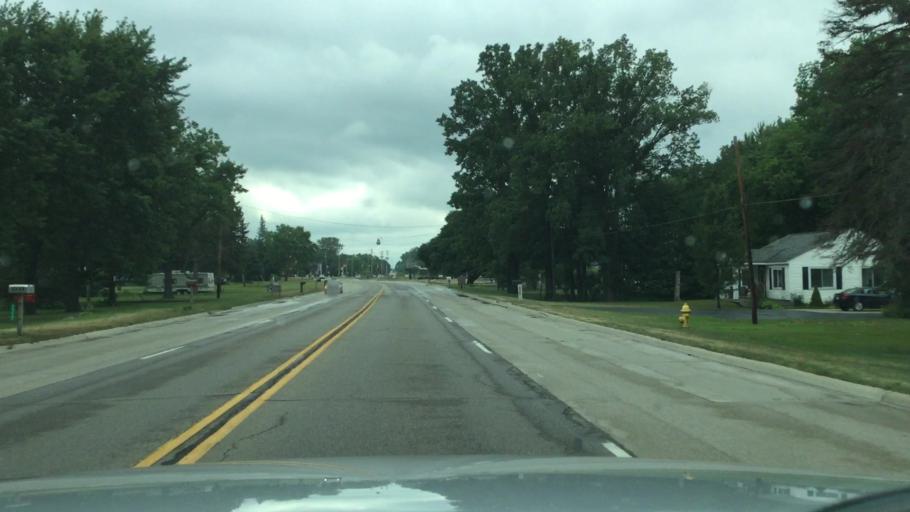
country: US
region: Michigan
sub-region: Genesee County
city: Burton
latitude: 43.0556
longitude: -83.6162
